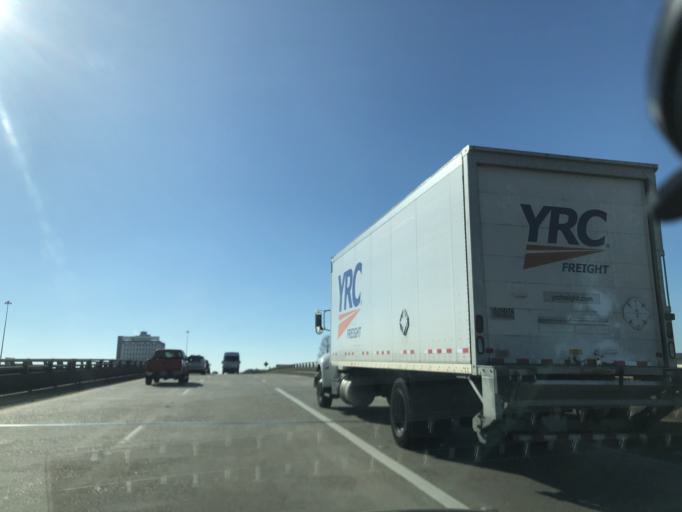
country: US
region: Louisiana
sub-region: Jefferson Parish
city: Metairie
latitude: 29.9984
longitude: -90.1554
